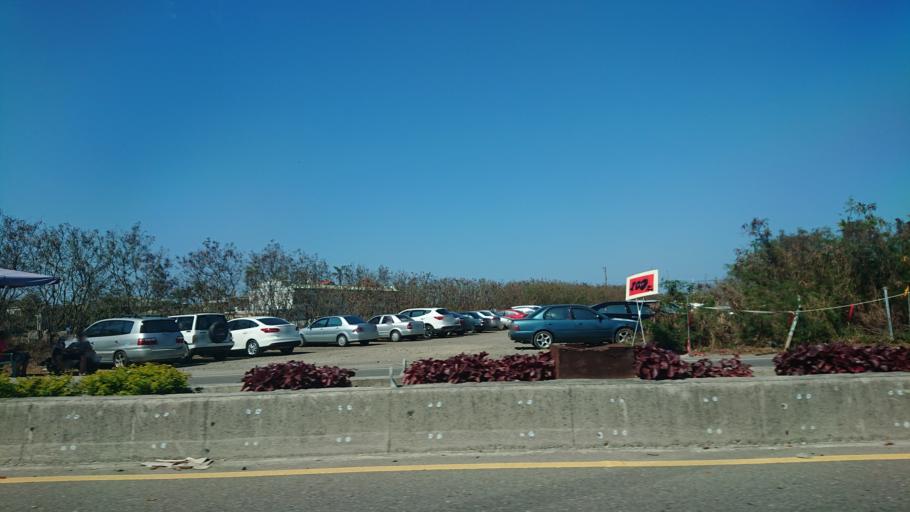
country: TW
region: Taiwan
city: Xinying
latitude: 23.2855
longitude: 120.1393
